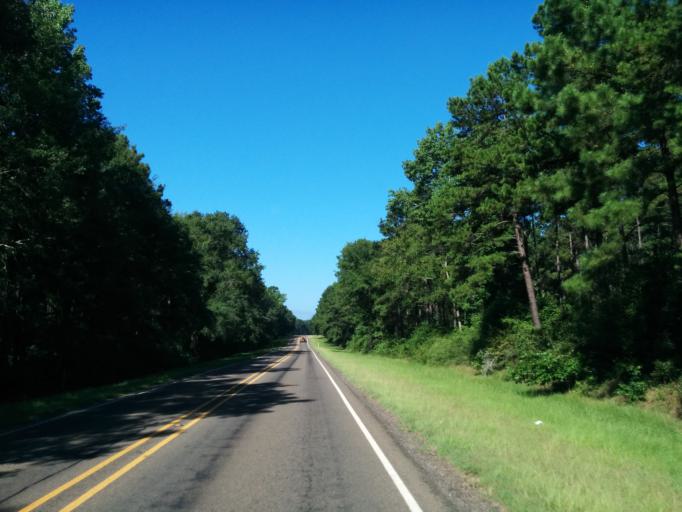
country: US
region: Texas
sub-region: Sabine County
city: Milam
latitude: 31.4323
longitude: -93.7921
